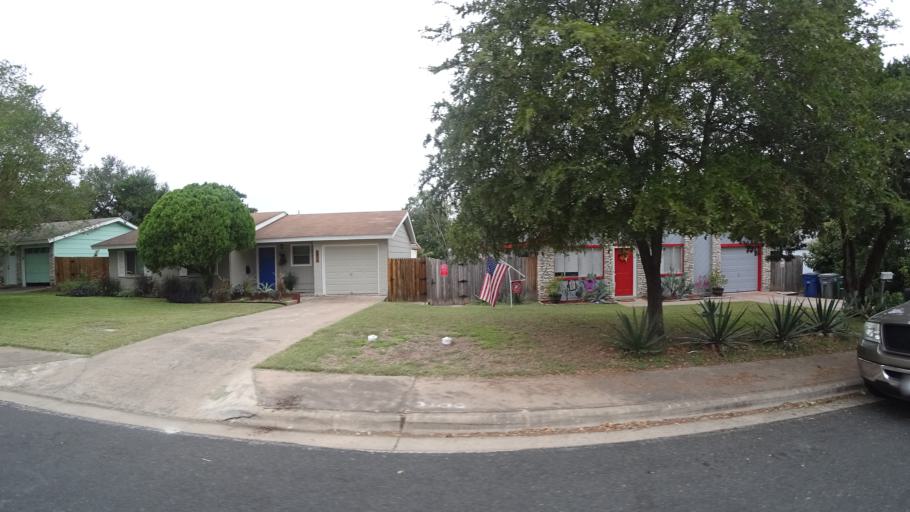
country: US
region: Texas
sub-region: Travis County
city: Onion Creek
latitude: 30.2039
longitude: -97.7799
